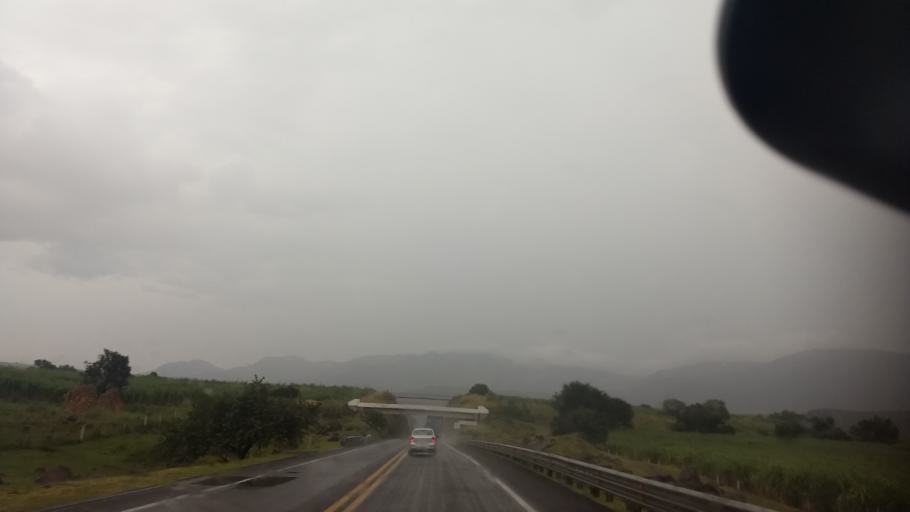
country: MX
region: Jalisco
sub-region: Tonila
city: San Marcos
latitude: 19.4364
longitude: -103.4804
